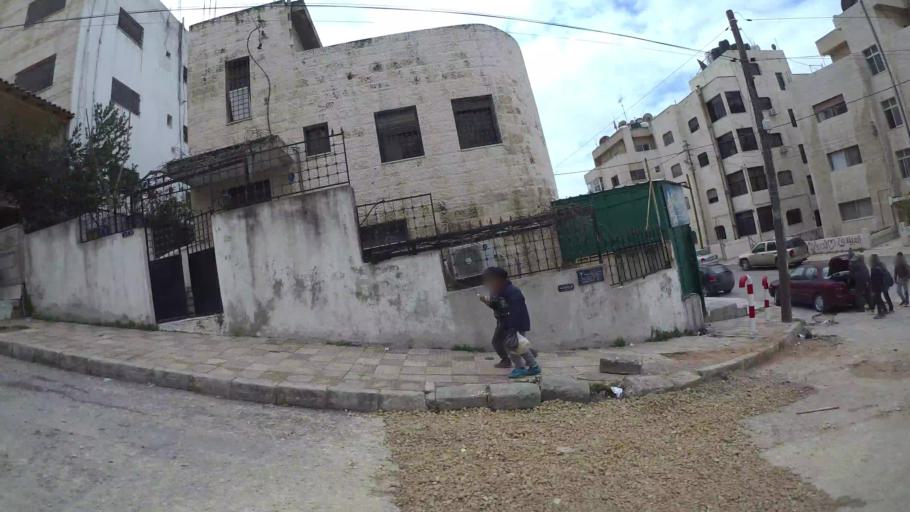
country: JO
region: Amman
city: Wadi as Sir
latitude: 31.9519
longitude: 35.8246
